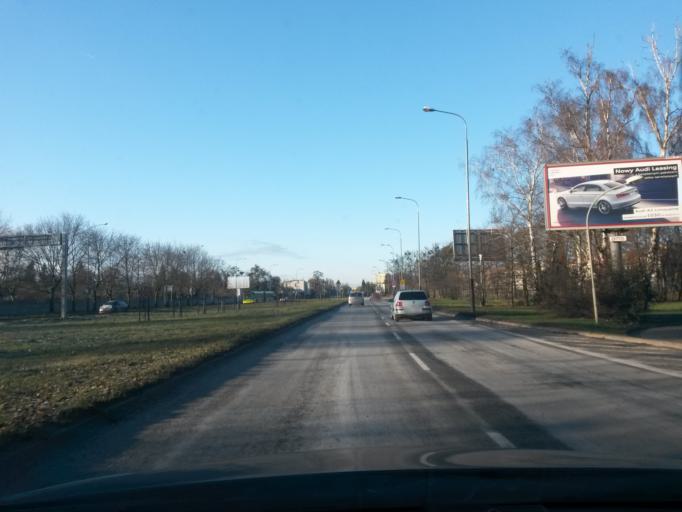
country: PL
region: Greater Poland Voivodeship
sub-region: Poznan
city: Poznan
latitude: 52.3935
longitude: 16.8853
